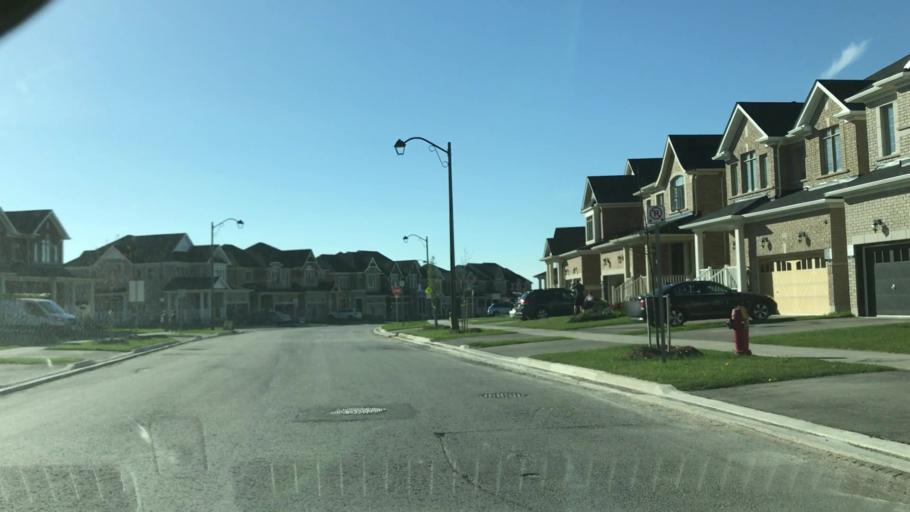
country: CA
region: Ontario
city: Newmarket
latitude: 44.0205
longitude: -79.4271
